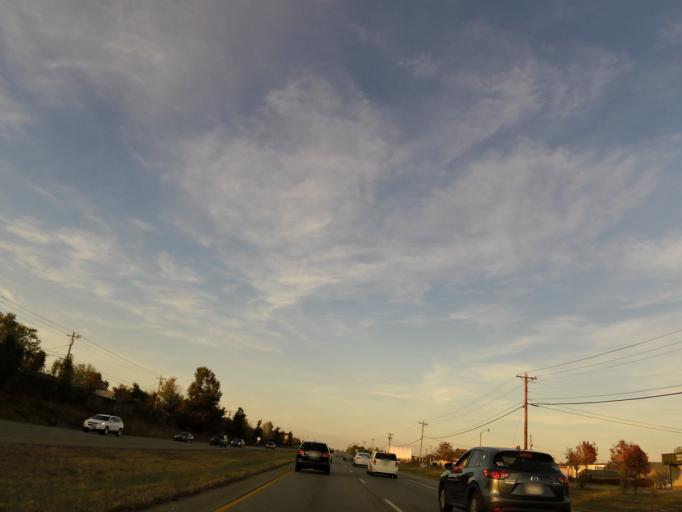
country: US
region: Kentucky
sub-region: Jessamine County
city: Nicholasville
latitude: 37.8897
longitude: -84.5906
